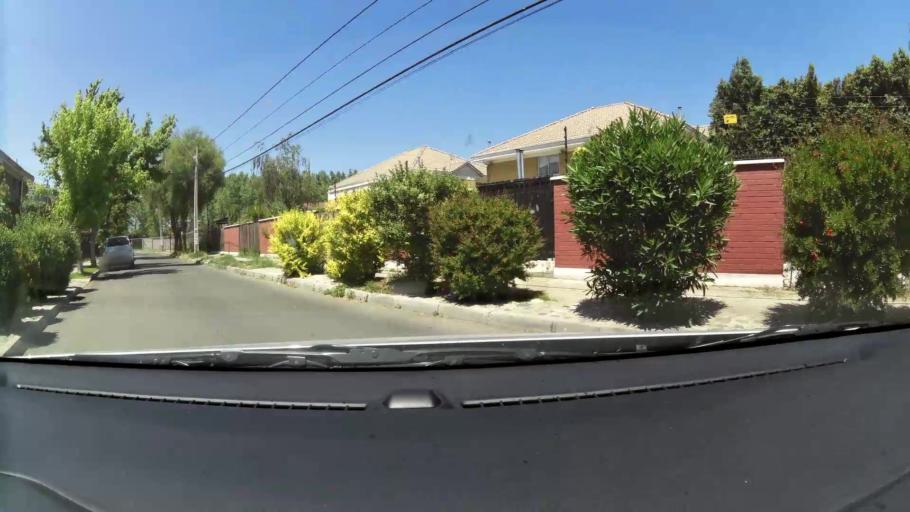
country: CL
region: Santiago Metropolitan
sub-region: Provincia de Maipo
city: San Bernardo
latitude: -33.6244
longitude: -70.7128
